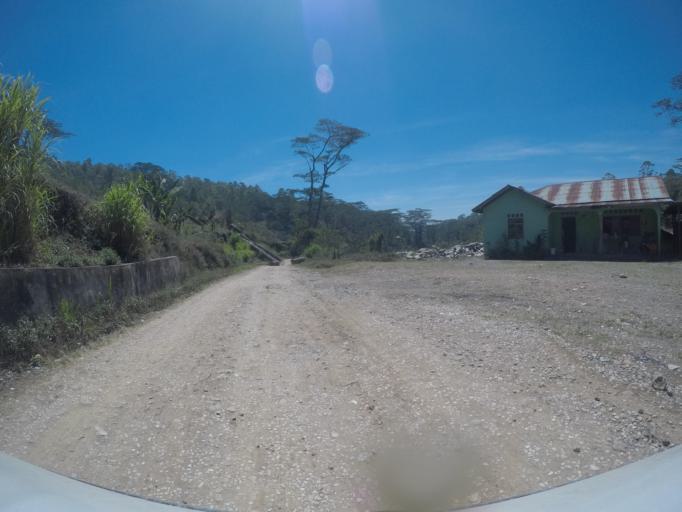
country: TL
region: Ermera
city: Gleno
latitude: -8.7740
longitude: 125.3978
